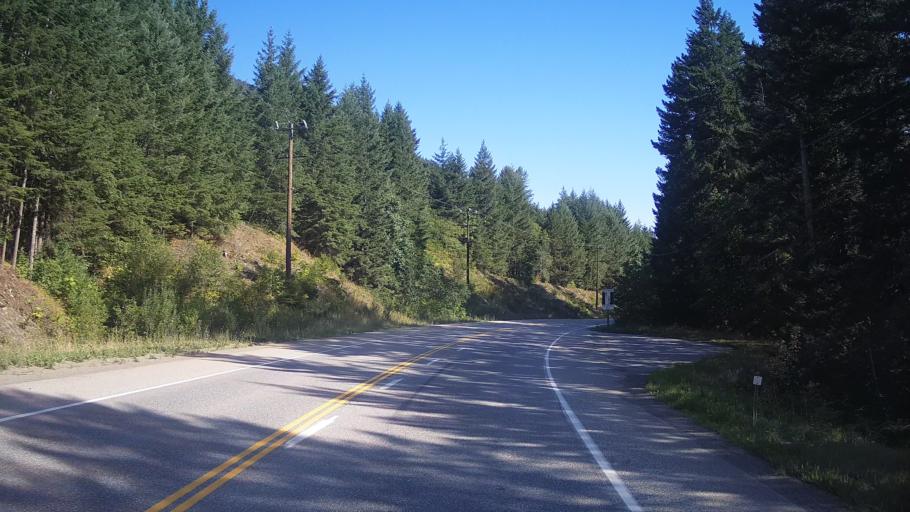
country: CA
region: British Columbia
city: Hope
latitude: 49.6666
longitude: -121.4200
